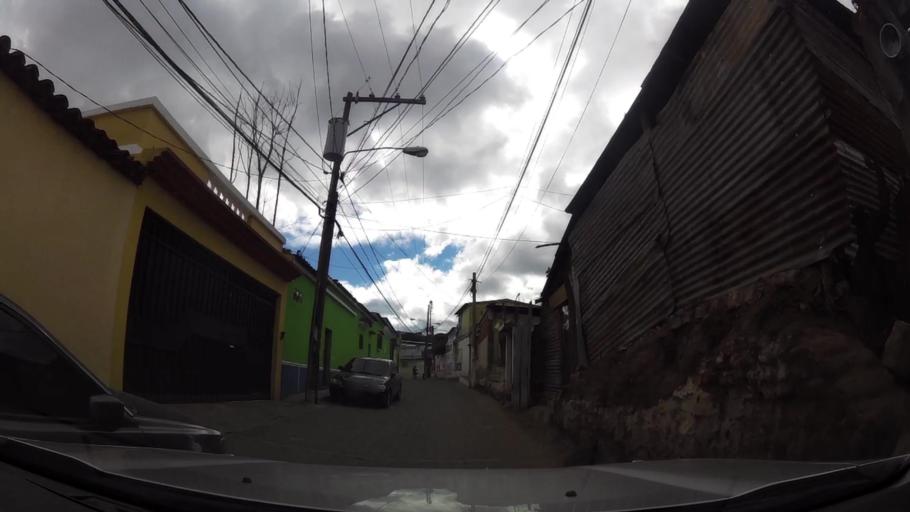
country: GT
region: Guatemala
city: Mixco
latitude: 14.6348
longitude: -90.6082
